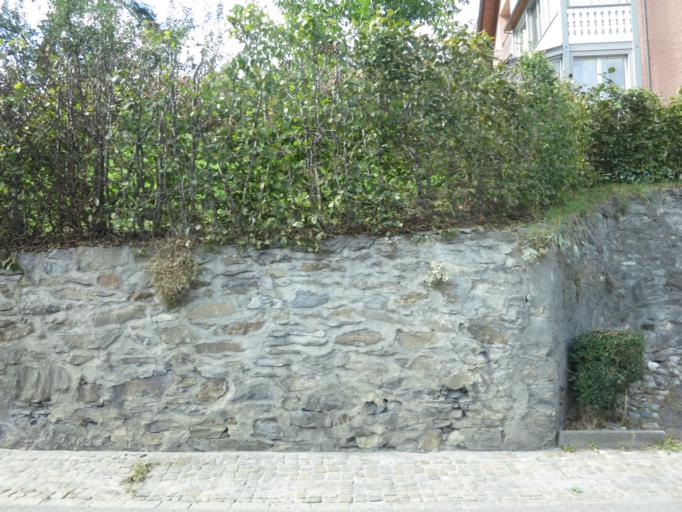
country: CH
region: Grisons
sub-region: Hinterrhein District
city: Thusis
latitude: 46.6991
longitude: 9.4397
